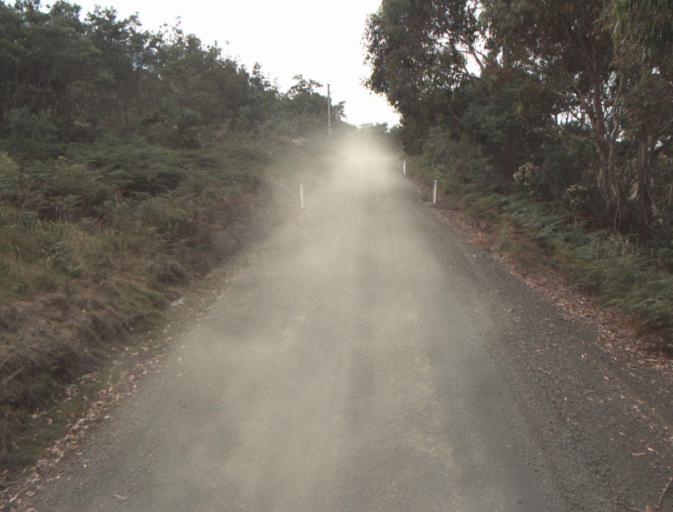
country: AU
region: Tasmania
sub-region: Northern Midlands
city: Evandale
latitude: -41.5185
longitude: 147.4146
